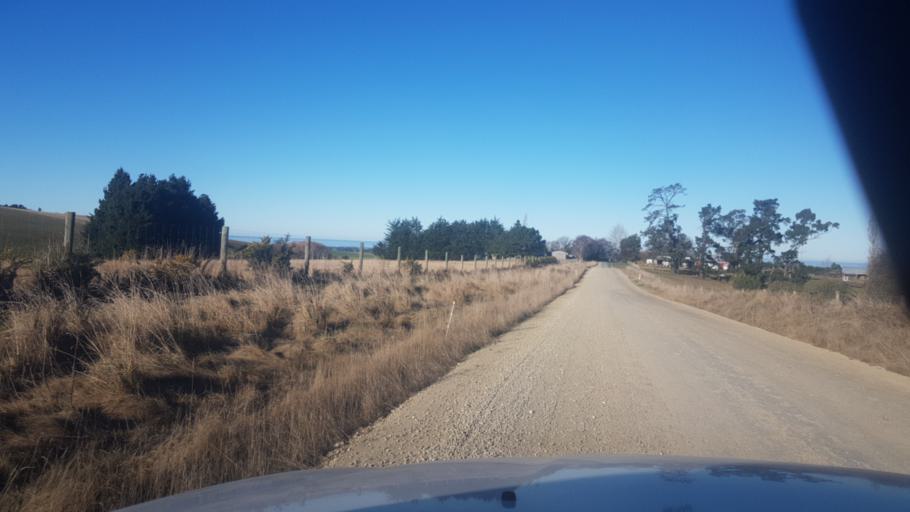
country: NZ
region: Canterbury
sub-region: Timaru District
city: Pleasant Point
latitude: -44.3710
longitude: 171.0748
